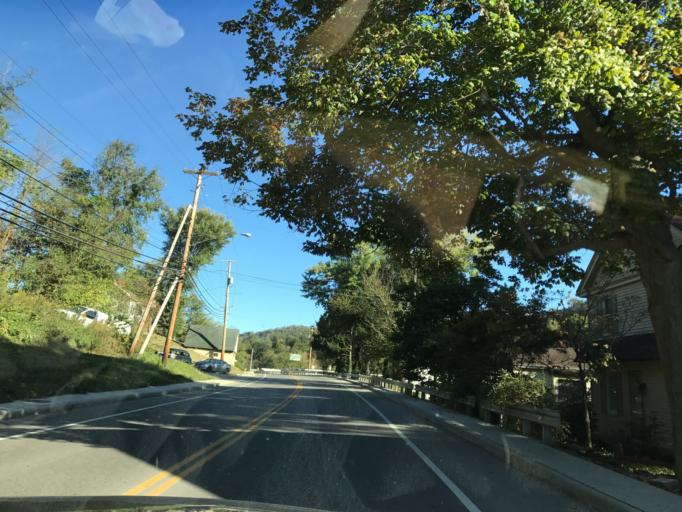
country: US
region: Ohio
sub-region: Belmont County
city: Wolfhurst
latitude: 40.0693
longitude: -80.7883
